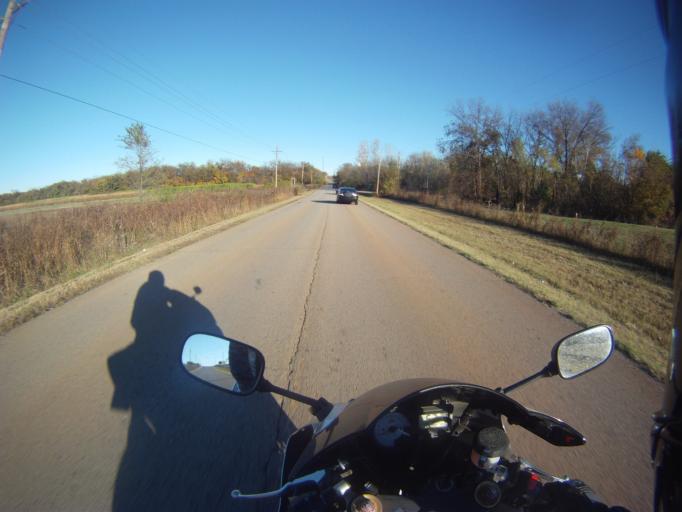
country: US
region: Oklahoma
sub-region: Payne County
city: Stillwater
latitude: 36.1303
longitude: -97.1067
